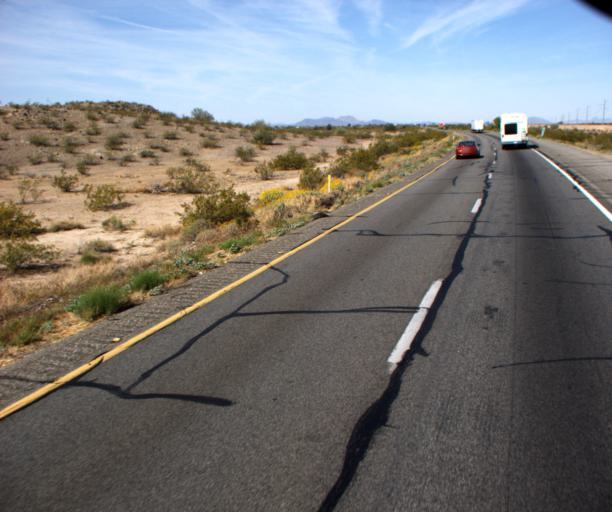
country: US
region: Arizona
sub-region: Maricopa County
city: Buckeye
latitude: 33.4333
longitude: -112.6437
